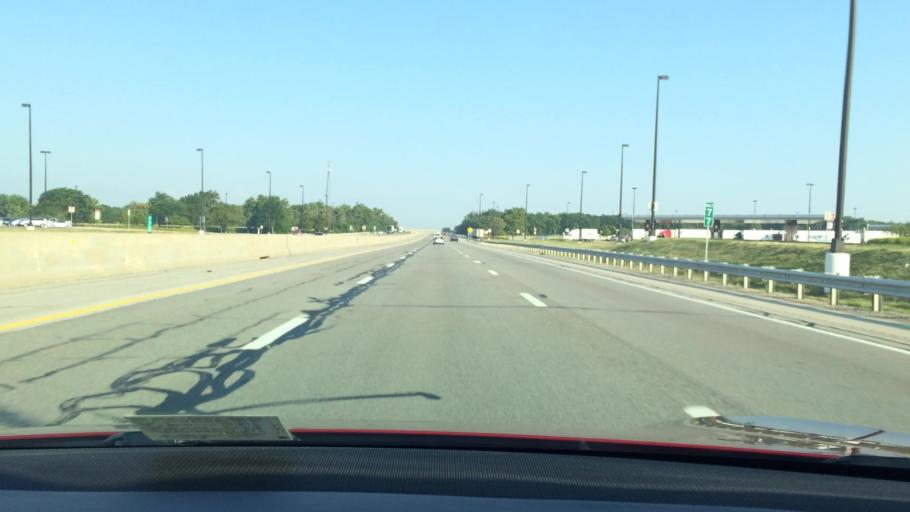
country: US
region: Ohio
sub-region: Ottawa County
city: Genoa
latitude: 41.4897
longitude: -83.3672
